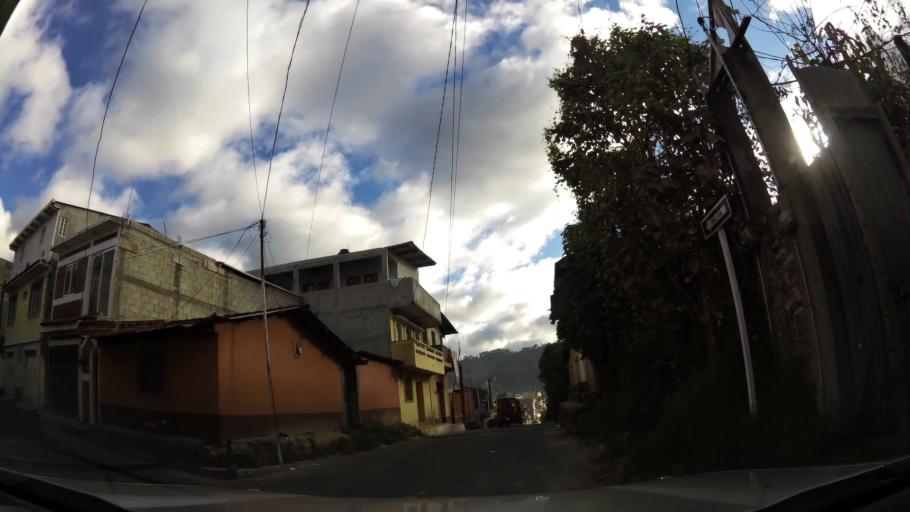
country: GT
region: Quiche
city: Chichicastenango
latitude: 14.9468
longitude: -91.1122
